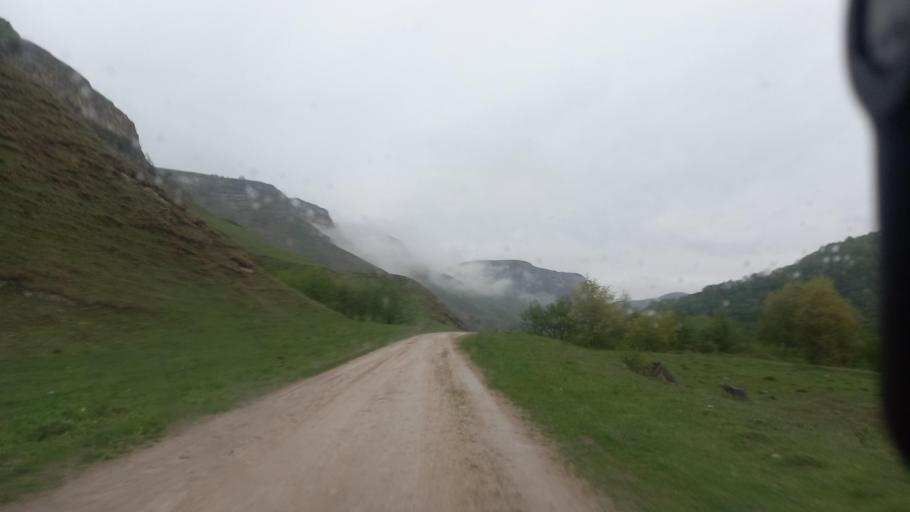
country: RU
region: Kabardino-Balkariya
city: Gundelen
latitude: 43.5976
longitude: 43.0635
